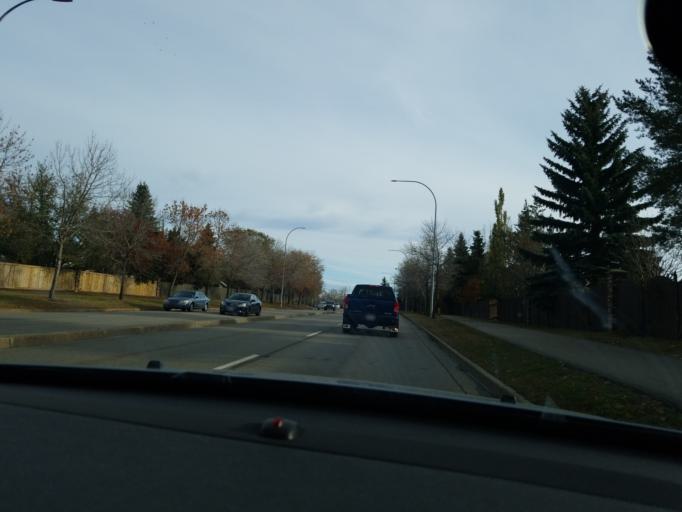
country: CA
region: Alberta
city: Sherwood Park
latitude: 53.5259
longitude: -113.2758
